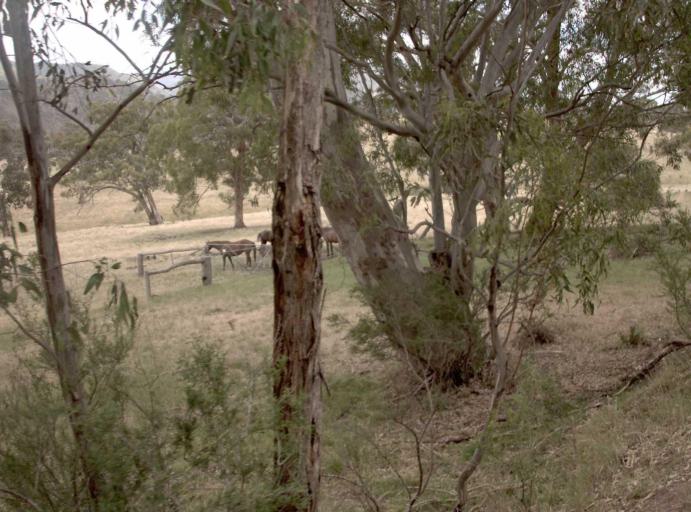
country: AU
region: Victoria
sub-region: Wellington
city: Heyfield
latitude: -37.6797
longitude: 146.6556
